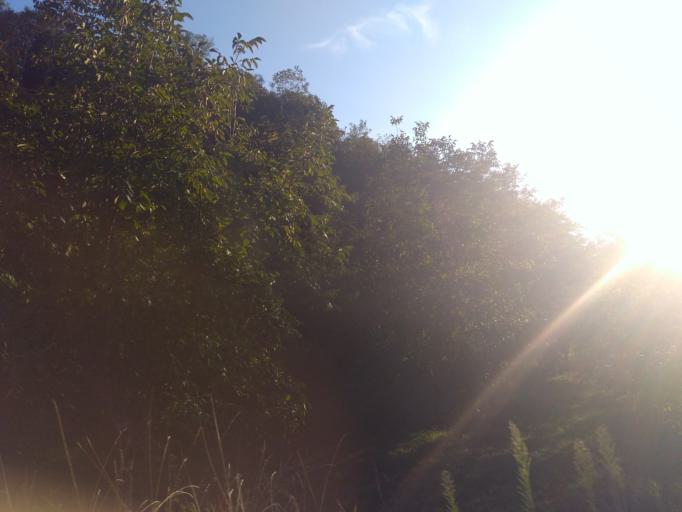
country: FR
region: Aquitaine
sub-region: Departement de la Dordogne
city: Domme
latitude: 44.8067
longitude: 1.2339
